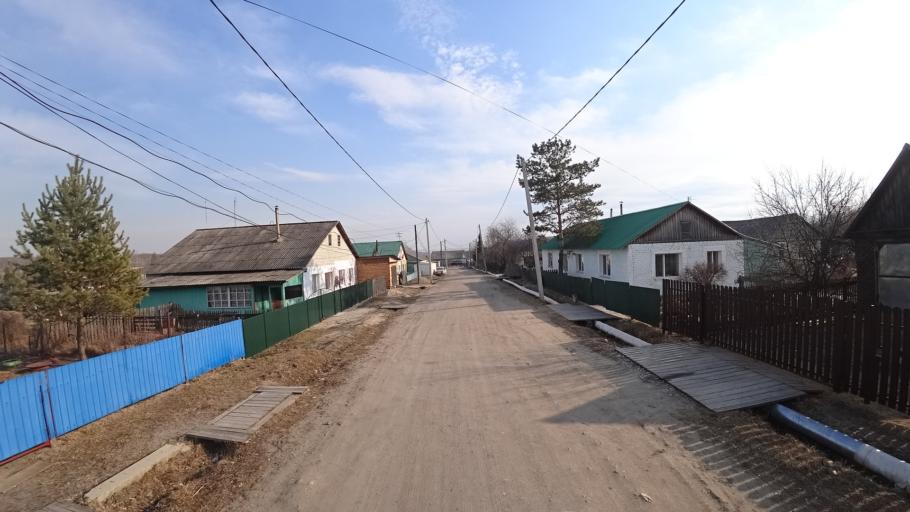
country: RU
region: Amur
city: Novobureyskiy
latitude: 49.8982
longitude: 129.8756
